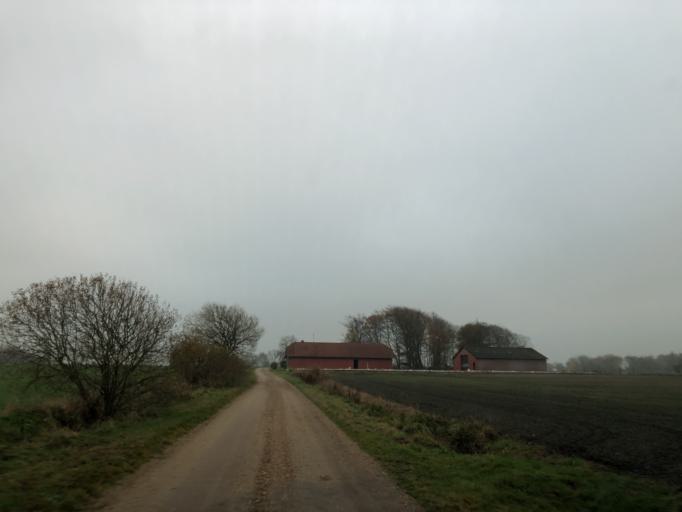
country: DK
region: Central Jutland
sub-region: Herning Kommune
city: Vildbjerg
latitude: 56.2087
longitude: 8.7251
